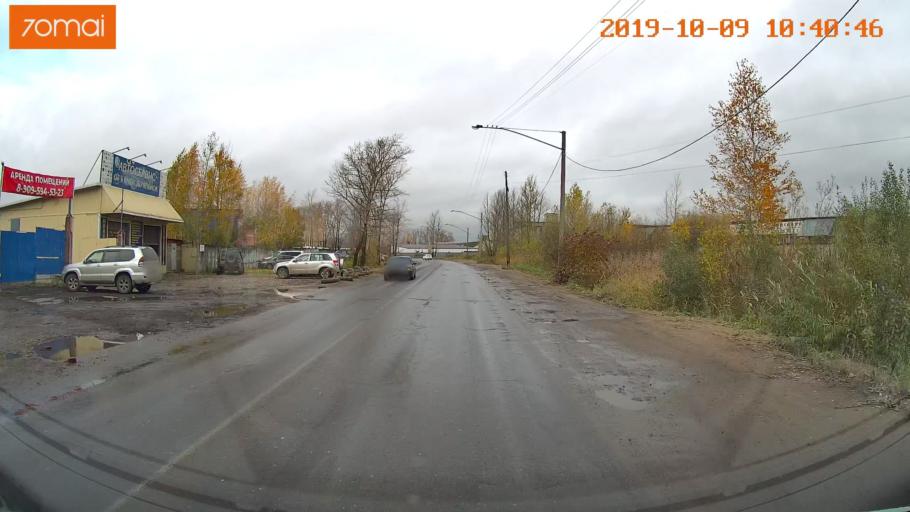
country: RU
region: Vologda
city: Vologda
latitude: 59.2337
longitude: 39.8353
